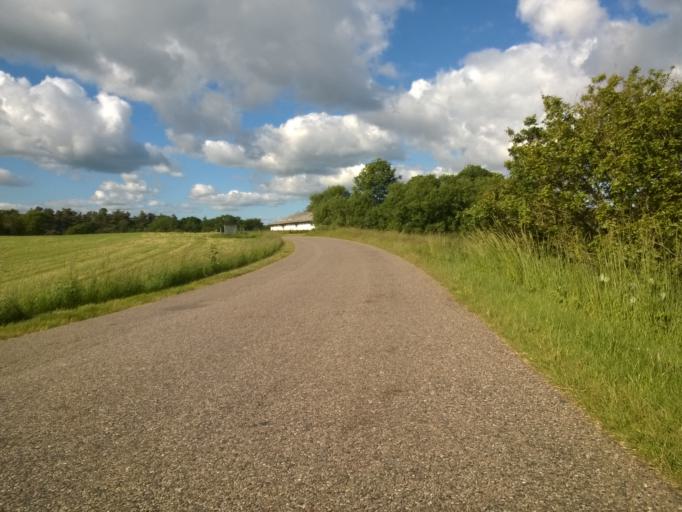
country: DK
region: Central Jutland
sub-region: Holstebro Kommune
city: Vinderup
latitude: 56.4778
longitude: 8.8629
